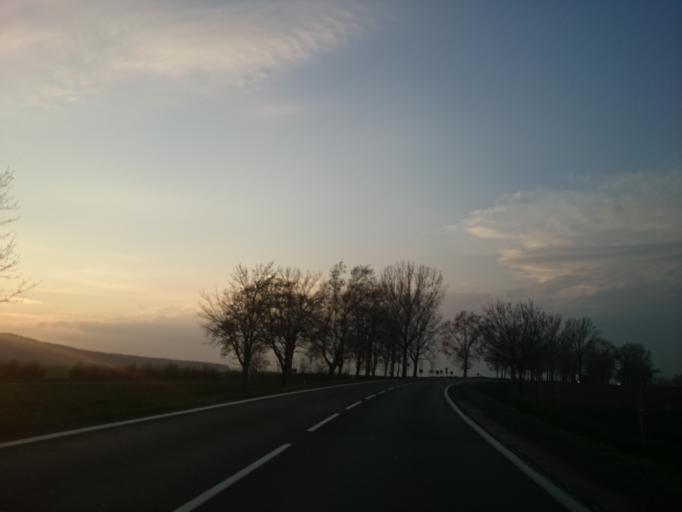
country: PL
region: Lower Silesian Voivodeship
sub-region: Powiat zabkowicki
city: Zabkowice Slaskie
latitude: 50.5589
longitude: 16.7927
